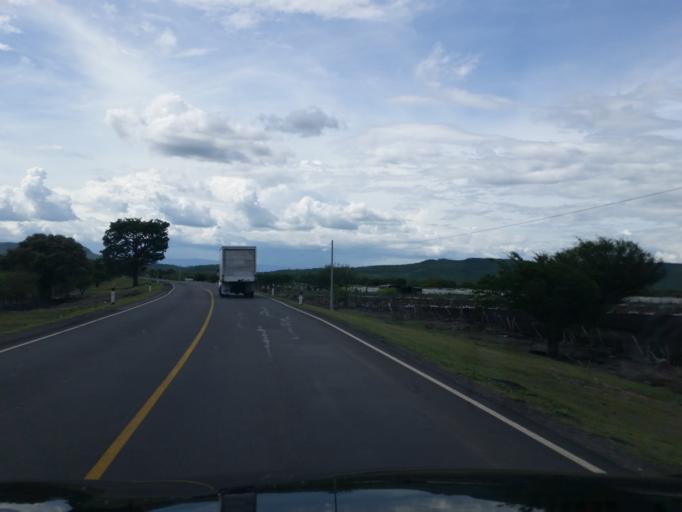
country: NI
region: Matagalpa
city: Ciudad Dario
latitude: 12.6394
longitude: -86.0626
